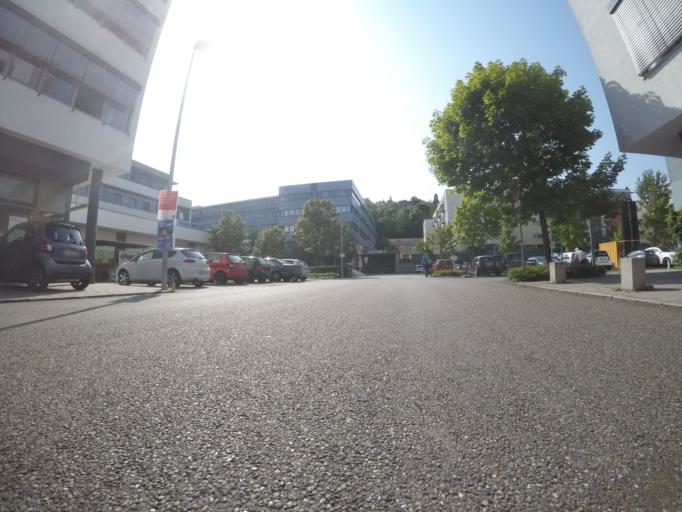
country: DE
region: Baden-Wuerttemberg
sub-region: Regierungsbezirk Stuttgart
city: Stuttgart Feuerbach
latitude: 48.8105
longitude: 9.1650
